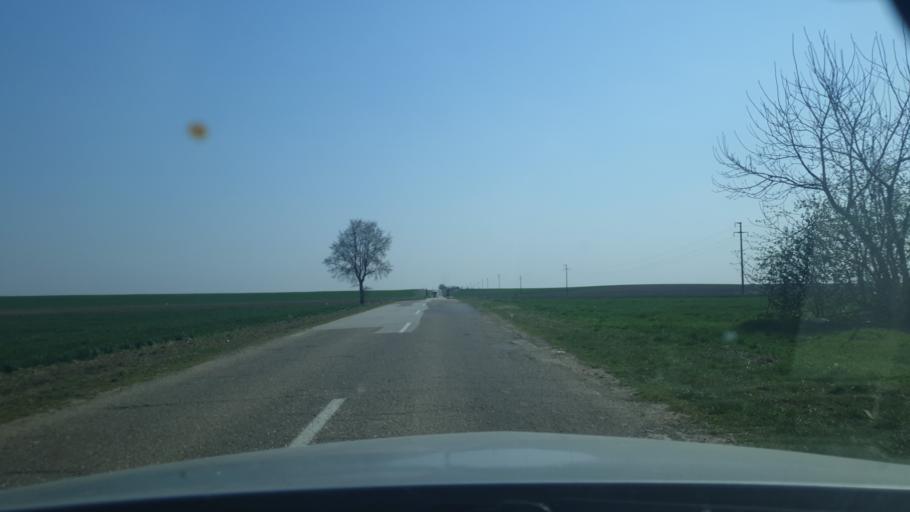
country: RS
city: Sasinci
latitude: 45.0393
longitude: 19.7349
